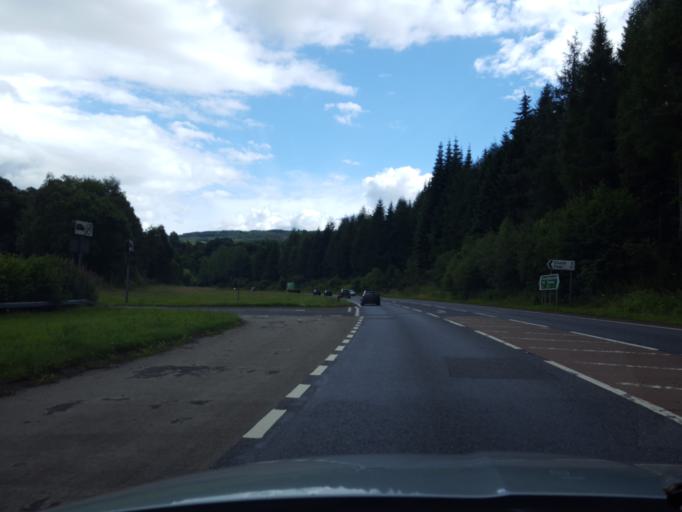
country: GB
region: Scotland
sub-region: Perth and Kinross
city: Pitlochry
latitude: 56.7017
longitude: -3.7507
